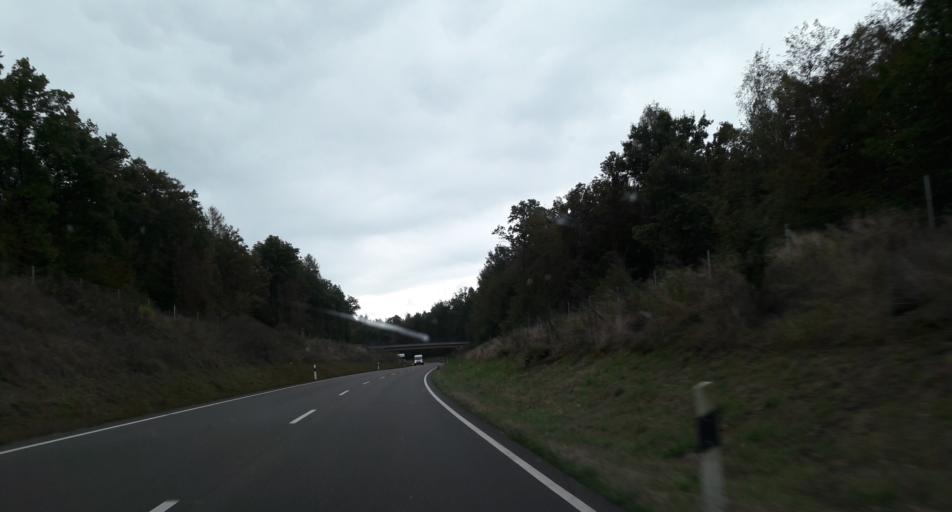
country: DE
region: Baden-Wuerttemberg
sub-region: Karlsruhe Region
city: Muhlhausen
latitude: 49.2417
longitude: 8.7176
